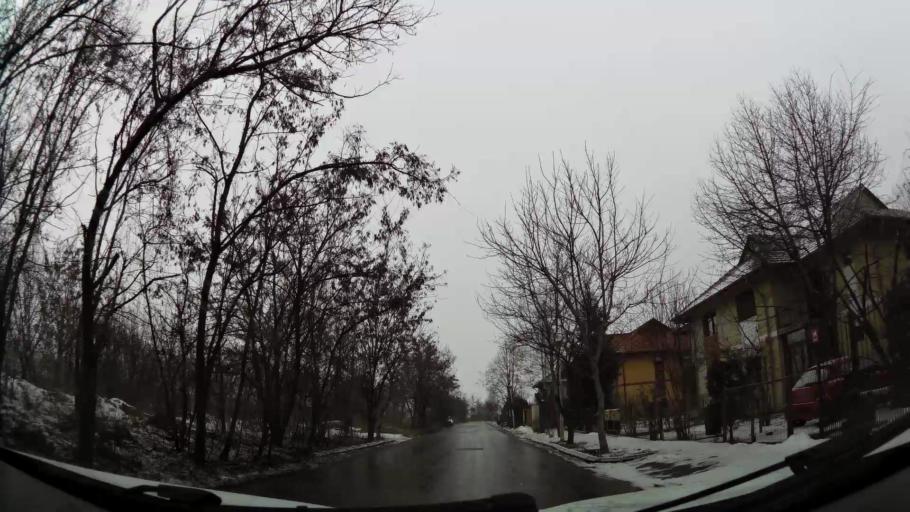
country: RO
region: Prahova
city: Ploiesti
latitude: 44.9597
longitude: 25.9978
